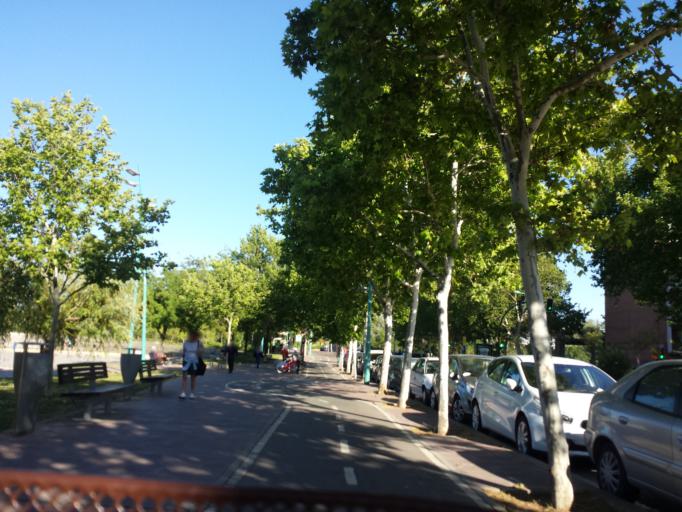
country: ES
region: Aragon
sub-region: Provincia de Zaragoza
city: Zaragoza
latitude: 41.6529
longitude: -0.8667
